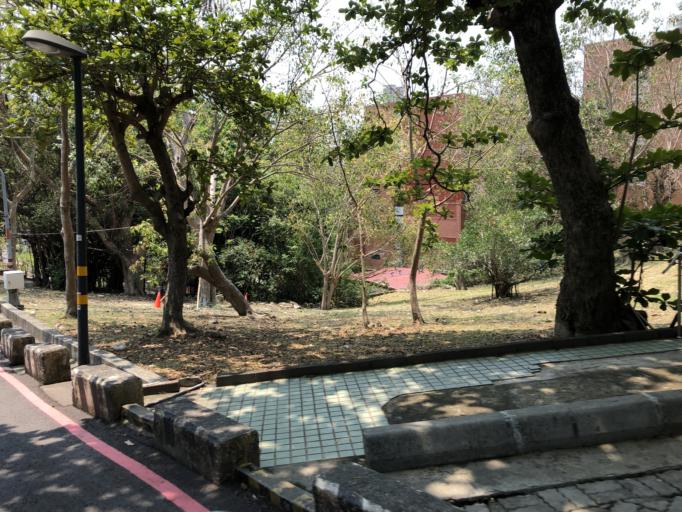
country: TW
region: Kaohsiung
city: Kaohsiung
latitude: 22.6290
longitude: 120.2695
